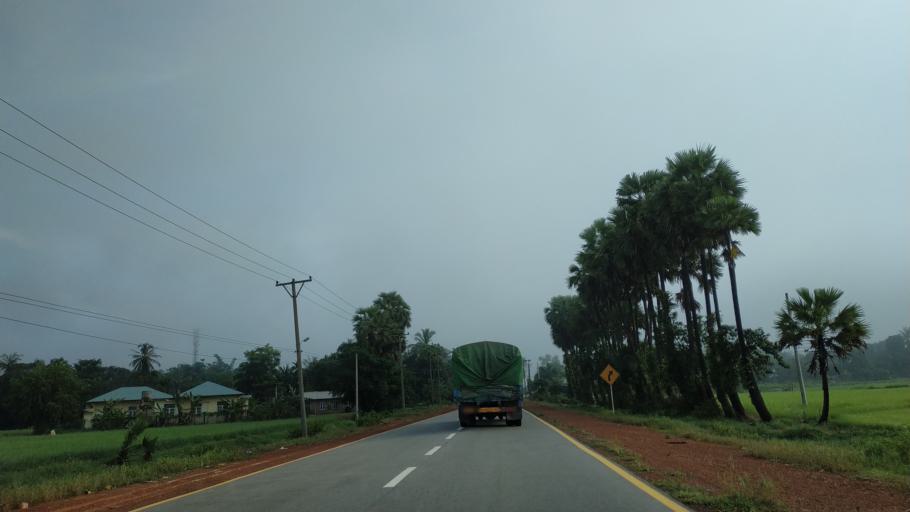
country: MM
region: Tanintharyi
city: Dawei
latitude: 14.1981
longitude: 98.2017
